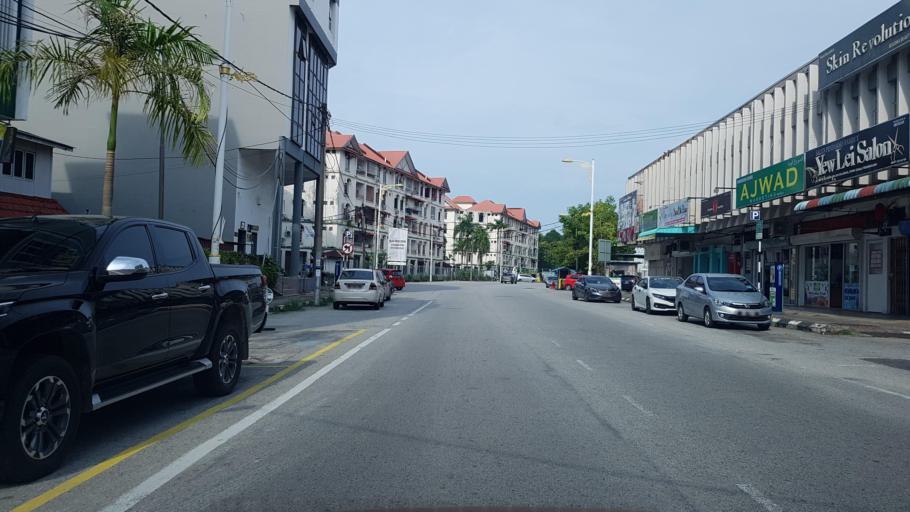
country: MY
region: Terengganu
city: Kuala Terengganu
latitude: 5.3339
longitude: 103.1399
